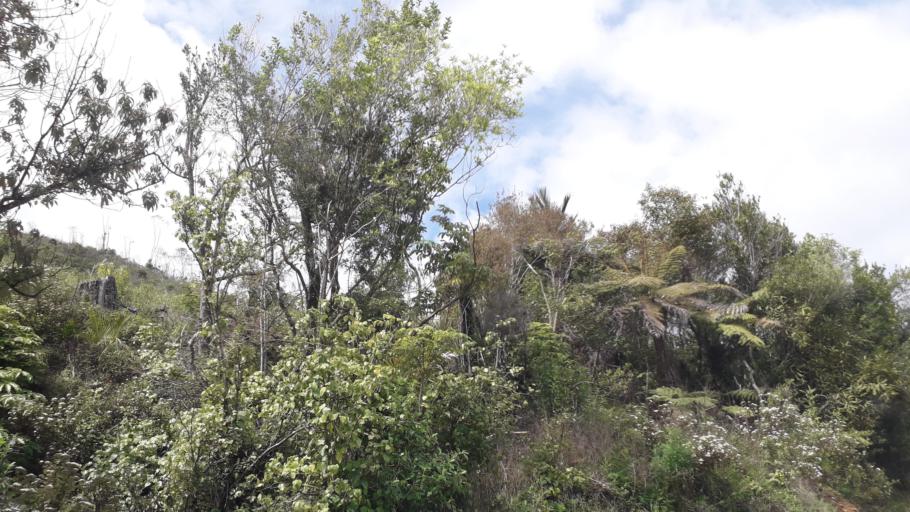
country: NZ
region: Northland
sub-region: Far North District
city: Taipa
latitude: -35.0941
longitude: 173.5369
